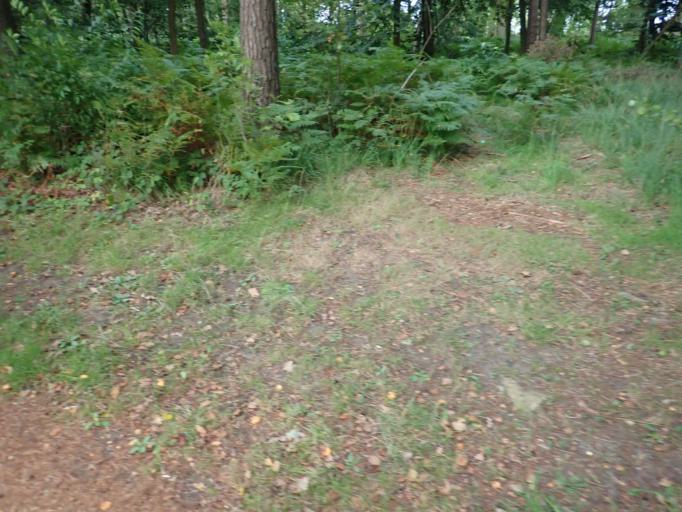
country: BE
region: Flanders
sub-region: Provincie Antwerpen
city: Oostmalle
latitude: 51.2844
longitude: 4.7694
